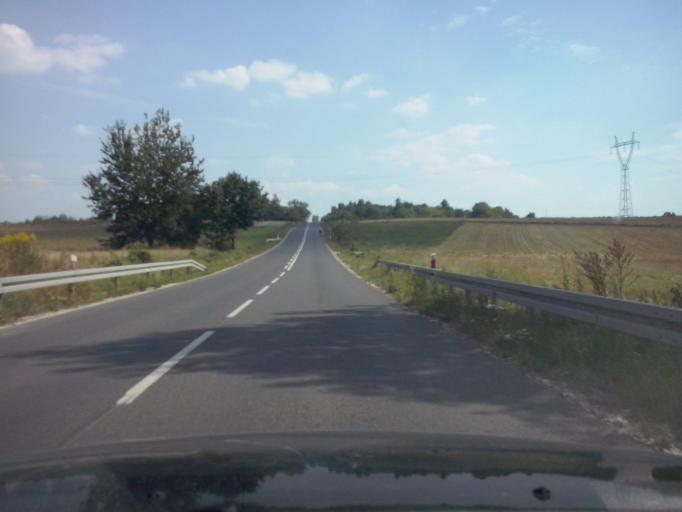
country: PL
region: Swietokrzyskie
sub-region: Powiat buski
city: Gnojno
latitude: 50.6062
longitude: 20.8267
